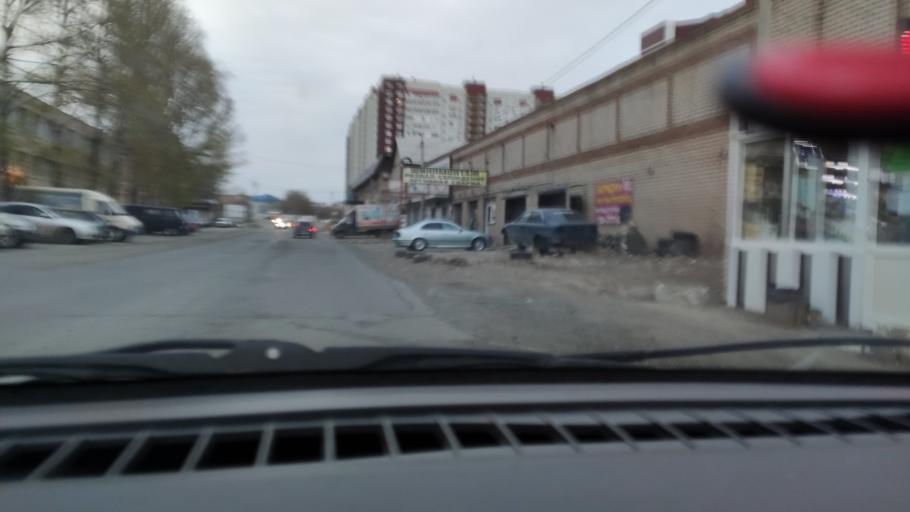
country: RU
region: Orenburg
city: Orenburg
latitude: 51.8143
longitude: 55.1498
